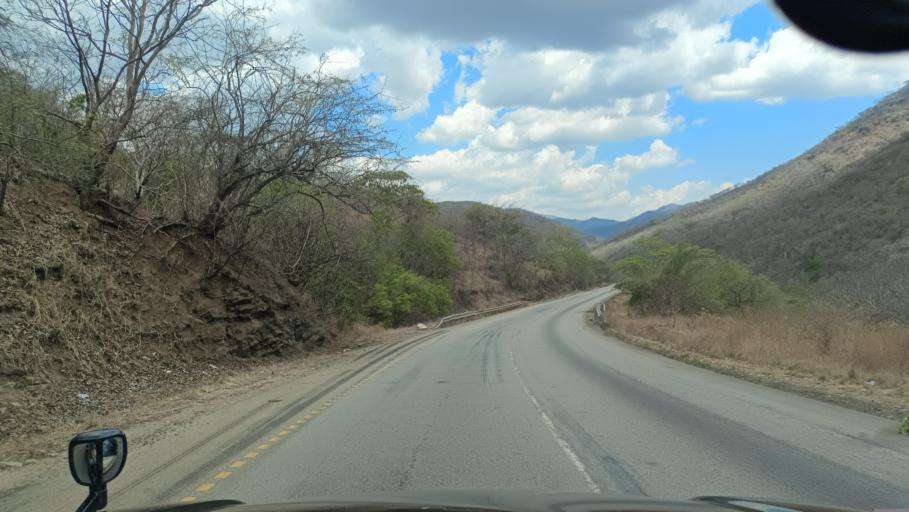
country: TZ
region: Morogoro
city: Kidatu
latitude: -7.5748
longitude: 36.7441
